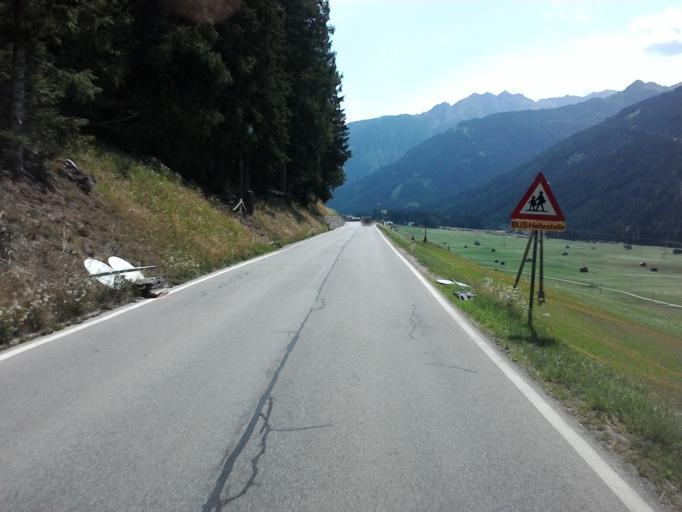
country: AT
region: Tyrol
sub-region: Politischer Bezirk Lienz
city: Obertilliach
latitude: 46.7090
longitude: 12.6247
